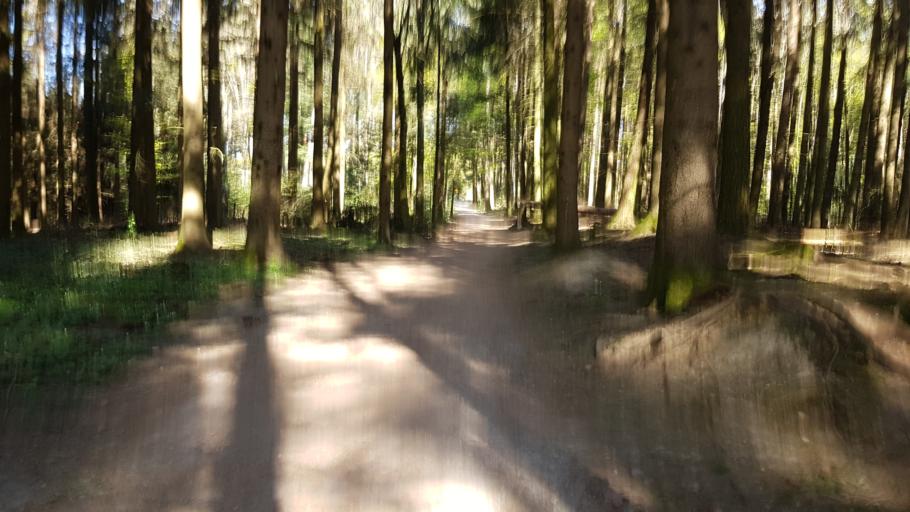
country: CH
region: Aargau
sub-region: Bezirk Kulm
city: Reinach
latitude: 47.2782
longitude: 8.1841
